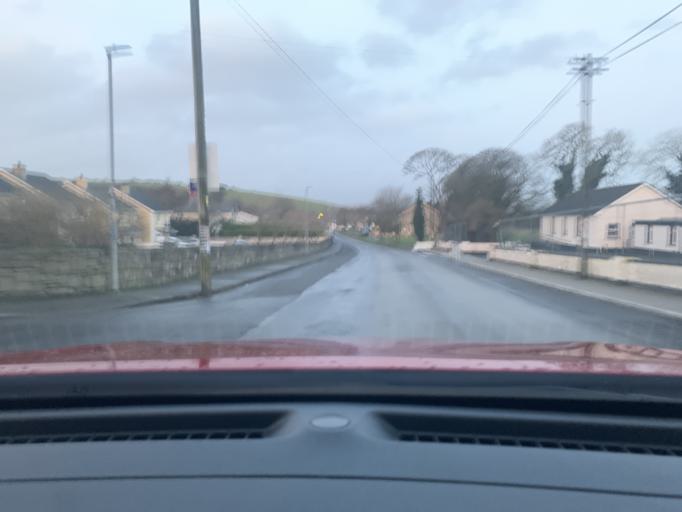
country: IE
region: Connaught
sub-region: Roscommon
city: Boyle
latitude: 54.0776
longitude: -8.3797
